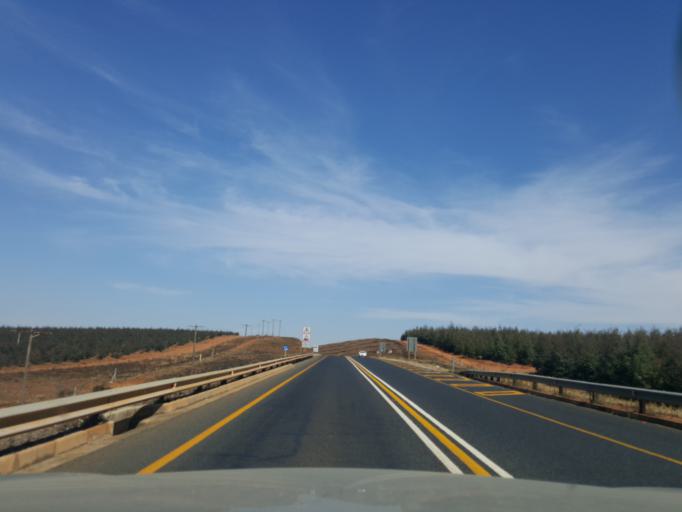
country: ZA
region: Mpumalanga
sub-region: Nkangala District Municipality
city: Belfast
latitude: -25.5787
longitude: 30.2934
